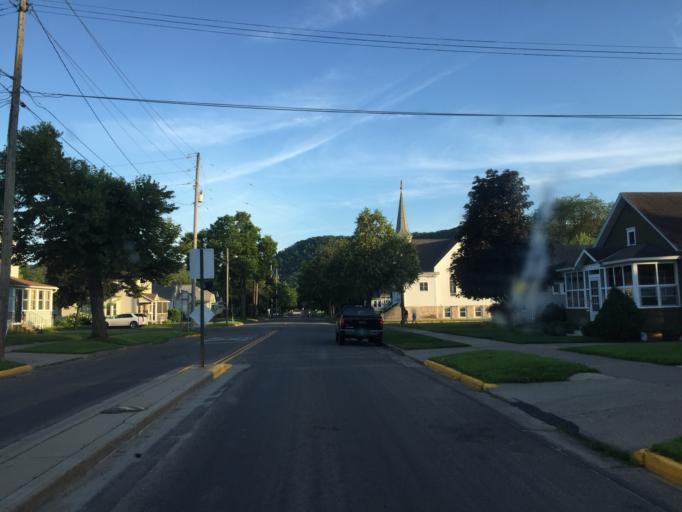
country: US
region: Minnesota
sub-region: Winona County
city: Winona
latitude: 44.0518
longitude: -91.6613
